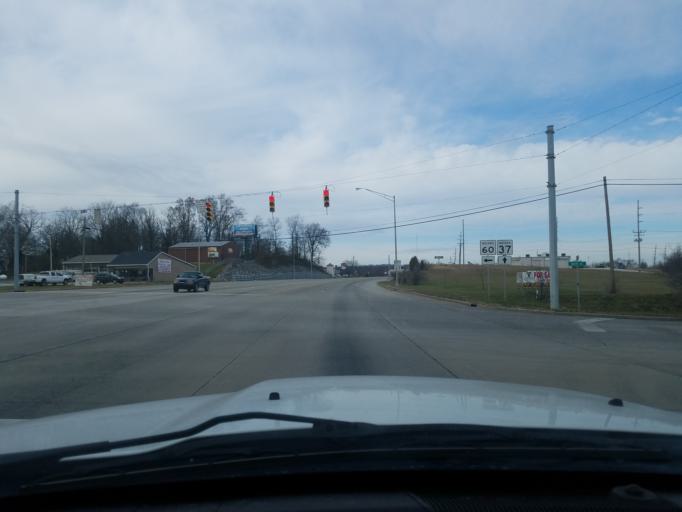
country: US
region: Indiana
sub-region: Lawrence County
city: Mitchell
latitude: 38.7314
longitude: -86.4895
